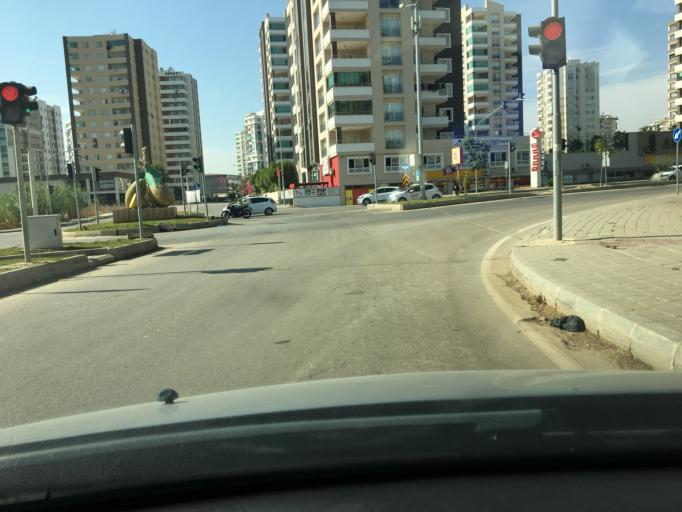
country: TR
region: Adana
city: Seyhan
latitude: 37.0197
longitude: 35.2587
